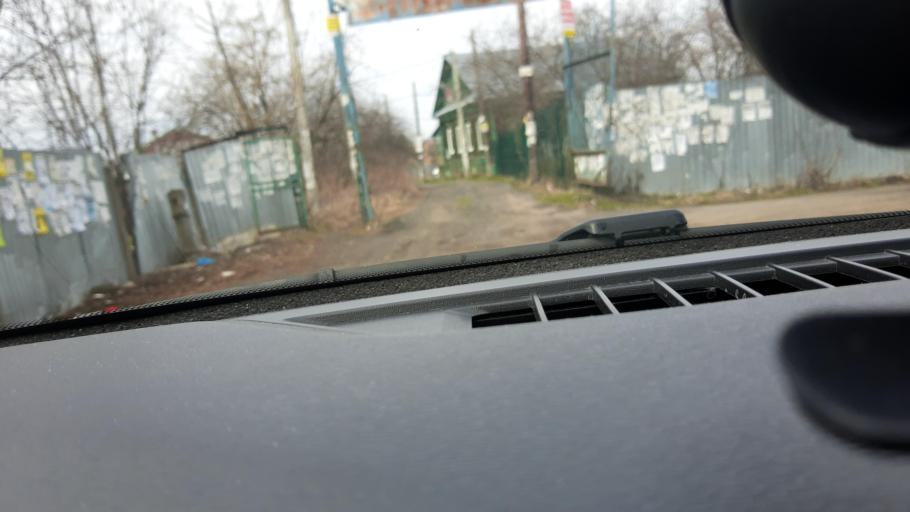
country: RU
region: Nizjnij Novgorod
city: Gorbatovka
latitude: 56.3834
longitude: 43.8208
